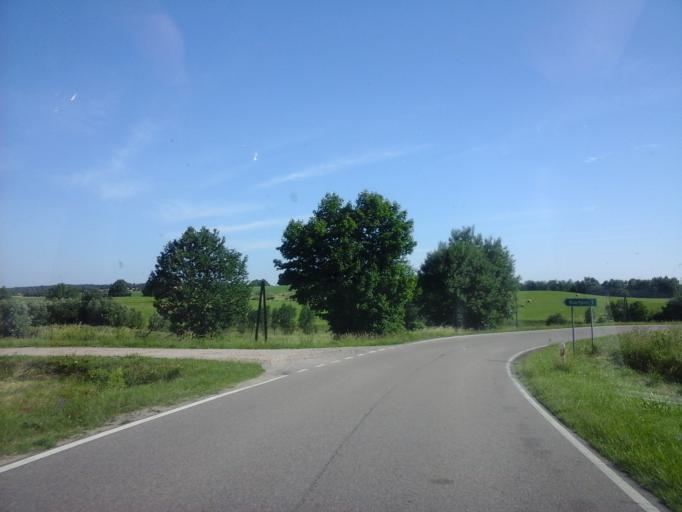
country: PL
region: West Pomeranian Voivodeship
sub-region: Powiat drawski
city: Zlocieniec
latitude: 53.6255
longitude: 15.9222
